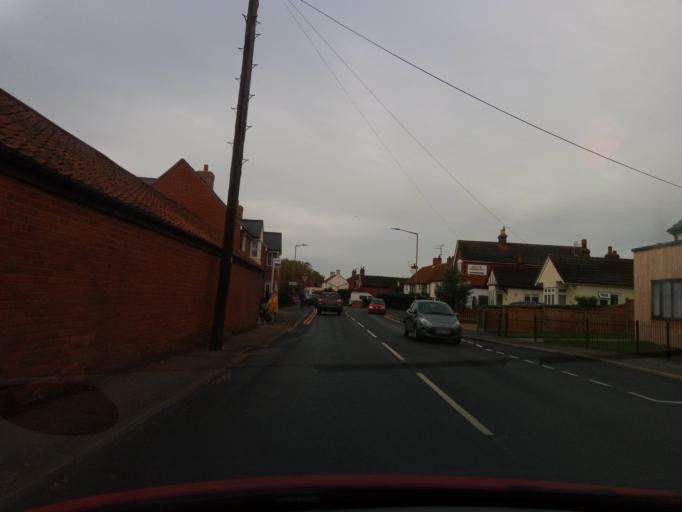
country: GB
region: England
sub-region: Essex
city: West Mersea
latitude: 51.7809
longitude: 0.9213
